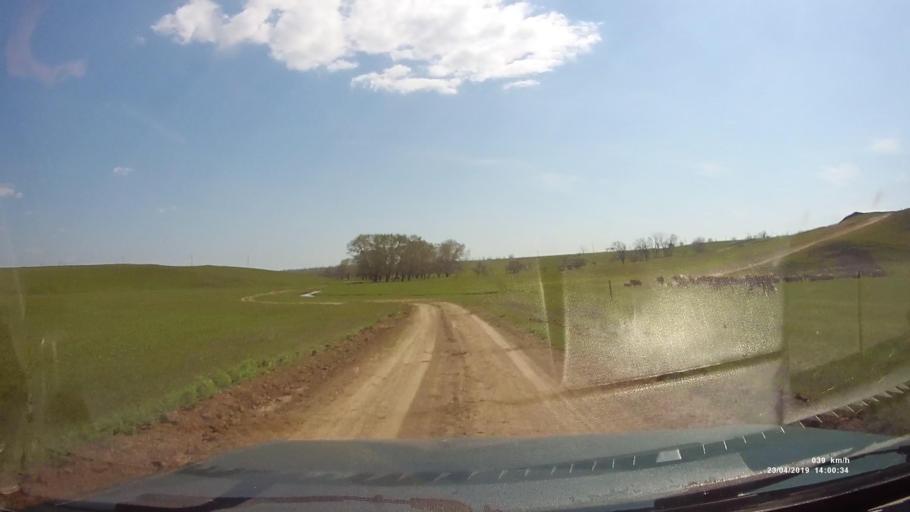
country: RU
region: Rostov
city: Remontnoye
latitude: 46.5588
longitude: 42.9469
